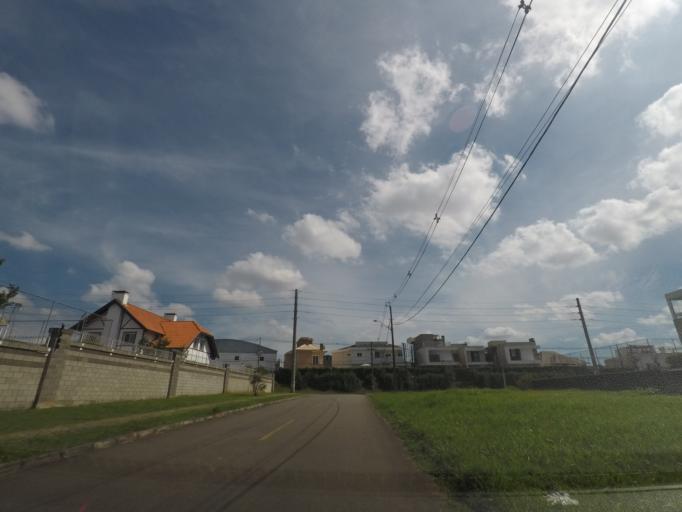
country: BR
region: Parana
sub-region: Curitiba
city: Curitiba
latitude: -25.4943
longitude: -49.2680
